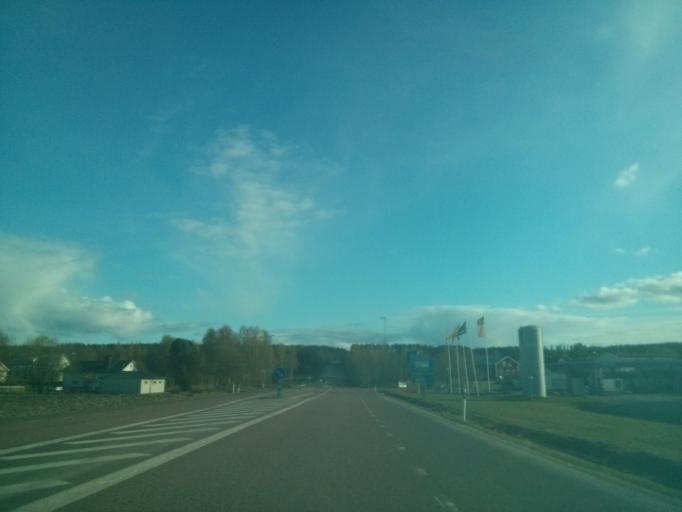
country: SE
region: Gaevleborg
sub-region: Nordanstigs Kommun
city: Bergsjoe
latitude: 62.0458
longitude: 17.2660
